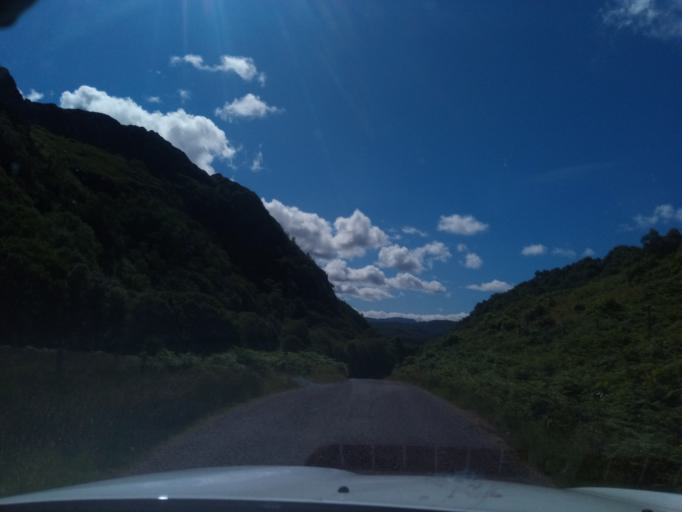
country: GB
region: Scotland
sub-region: Argyll and Bute
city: Isle Of Mull
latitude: 56.7726
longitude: -5.8246
